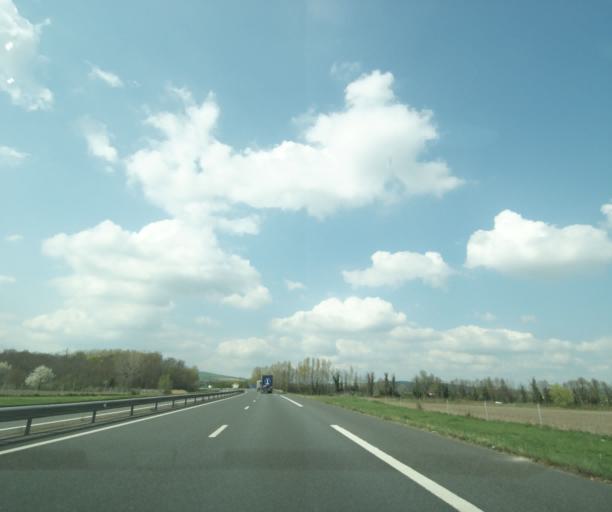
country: FR
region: Auvergne
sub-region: Departement du Puy-de-Dome
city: Saint-Bonnet-pres-Riom
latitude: 45.9452
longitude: 3.1220
